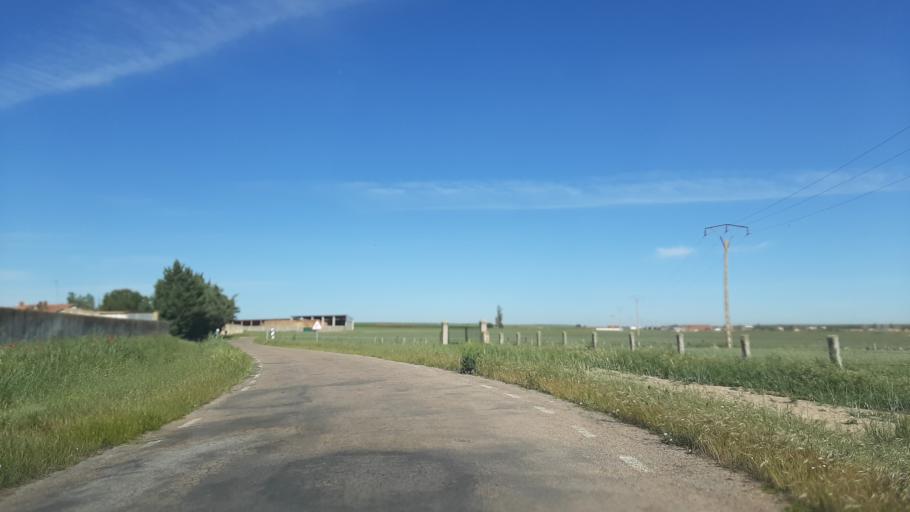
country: ES
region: Castille and Leon
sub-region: Provincia de Salamanca
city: Pedrosillo de Alba
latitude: 40.8098
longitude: -5.3818
